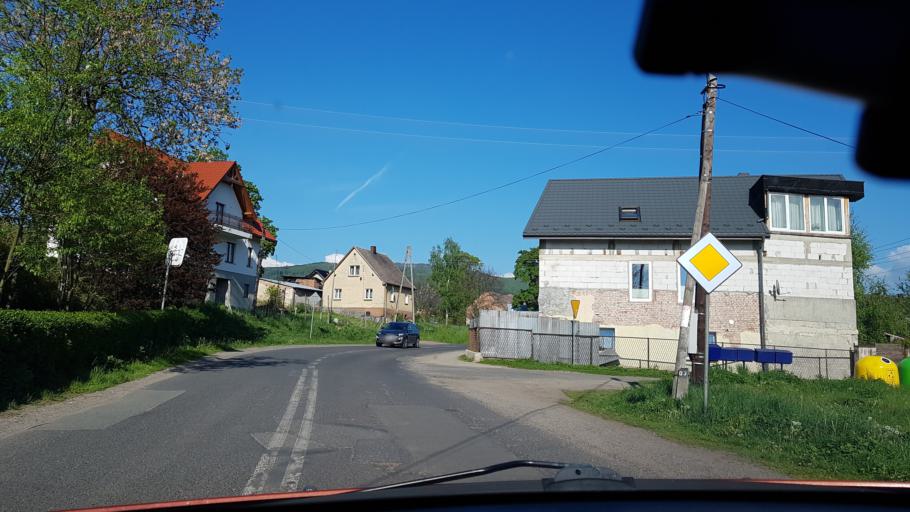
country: PL
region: Lower Silesian Voivodeship
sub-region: Powiat klodzki
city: Jugow
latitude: 50.5895
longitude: 16.5514
